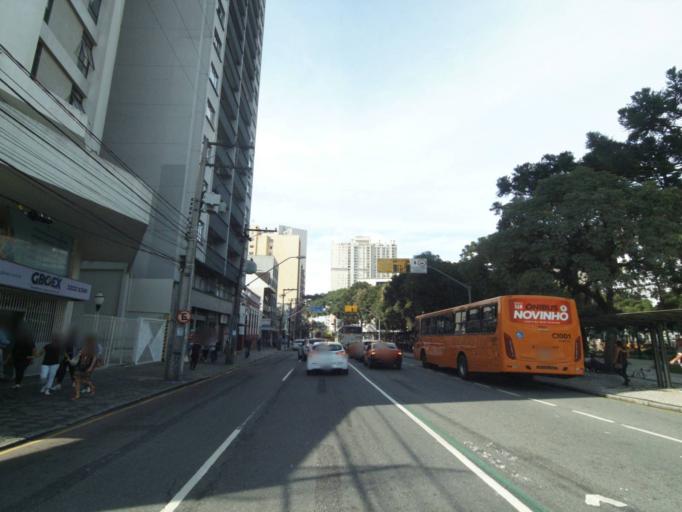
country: BR
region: Parana
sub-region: Curitiba
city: Curitiba
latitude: -25.4284
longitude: -49.2668
